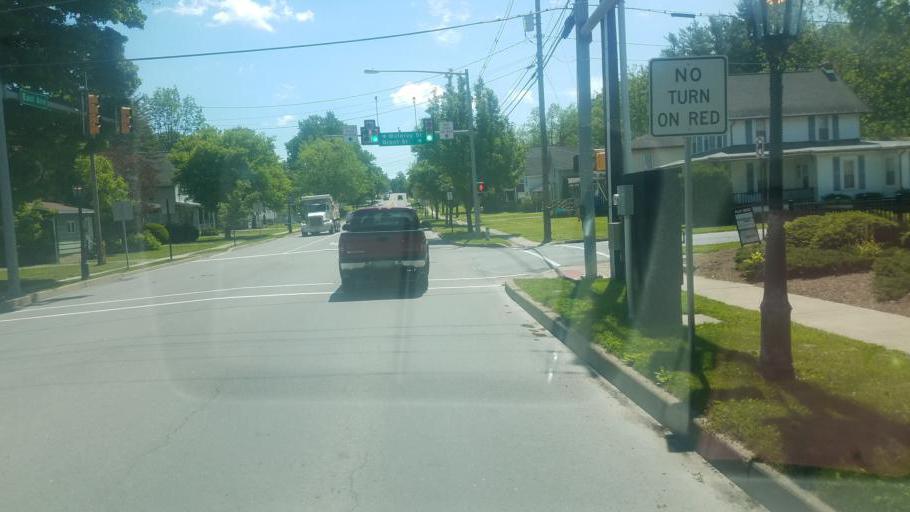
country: US
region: Pennsylvania
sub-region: Tioga County
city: Wellsboro
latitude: 41.7484
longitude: -77.2960
